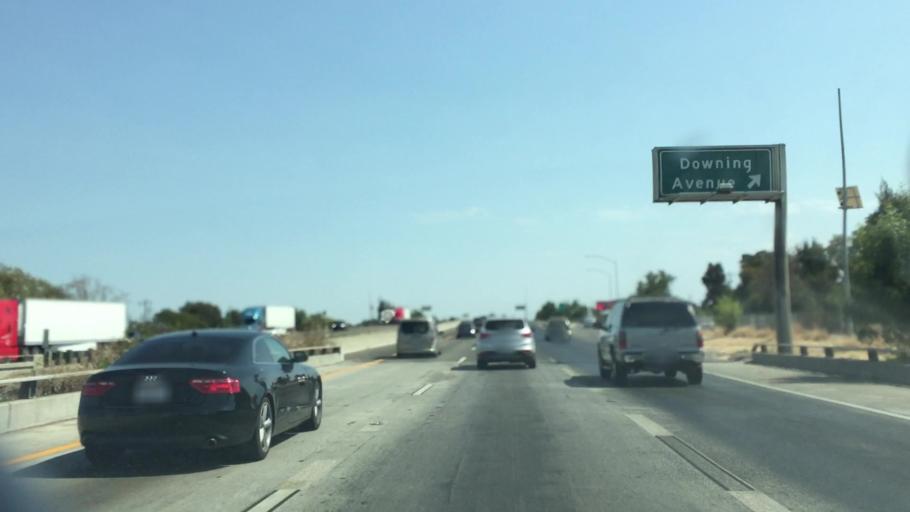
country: US
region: California
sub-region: San Joaquin County
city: Taft Mosswood
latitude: 37.9164
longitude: -121.2905
